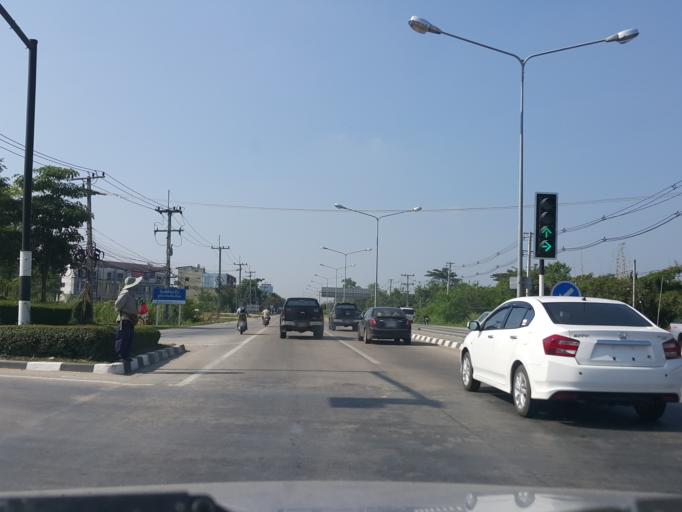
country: TH
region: Chiang Mai
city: San Sai
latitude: 18.8262
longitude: 99.0478
